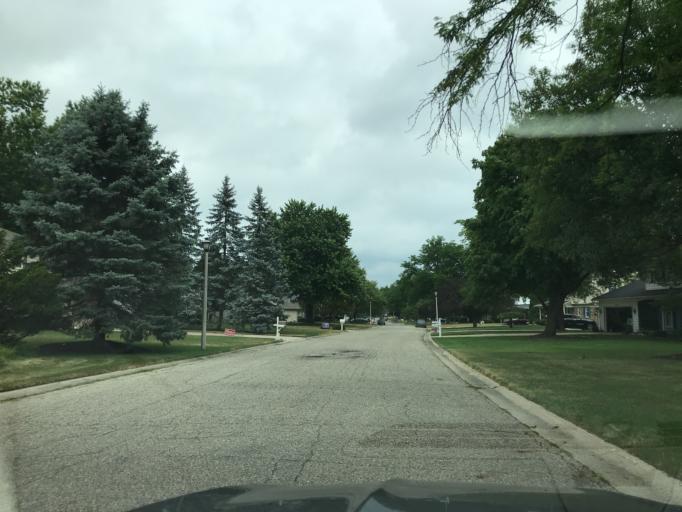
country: US
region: Michigan
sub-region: Eaton County
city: Waverly
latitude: 42.7568
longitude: -84.6281
